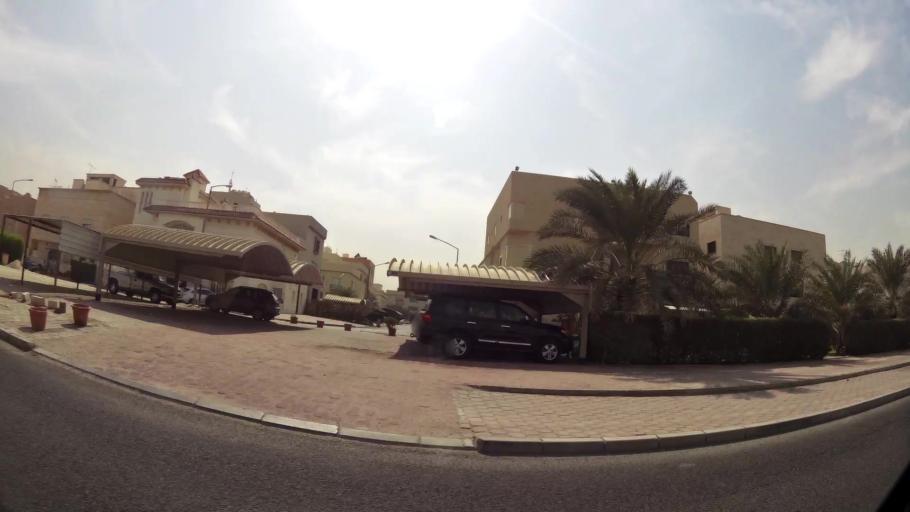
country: KW
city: Bayan
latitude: 29.2887
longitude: 48.0154
